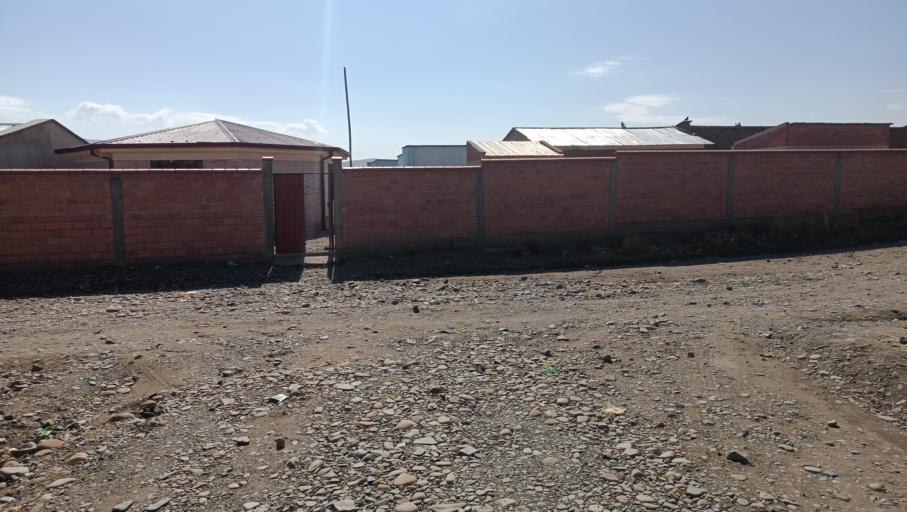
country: BO
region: La Paz
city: Batallas
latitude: -16.4386
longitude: -68.3719
